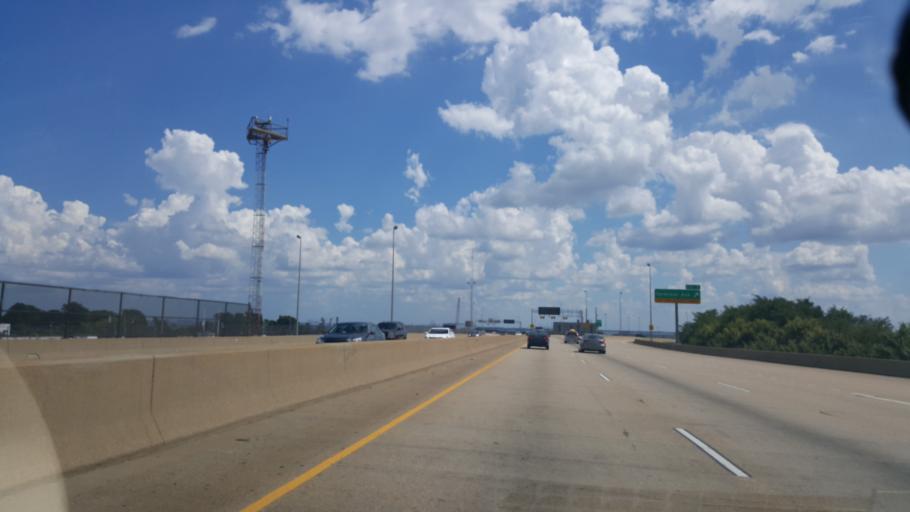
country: US
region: Virginia
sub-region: City of Newport News
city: Newport News
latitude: 36.9705
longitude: -76.4176
